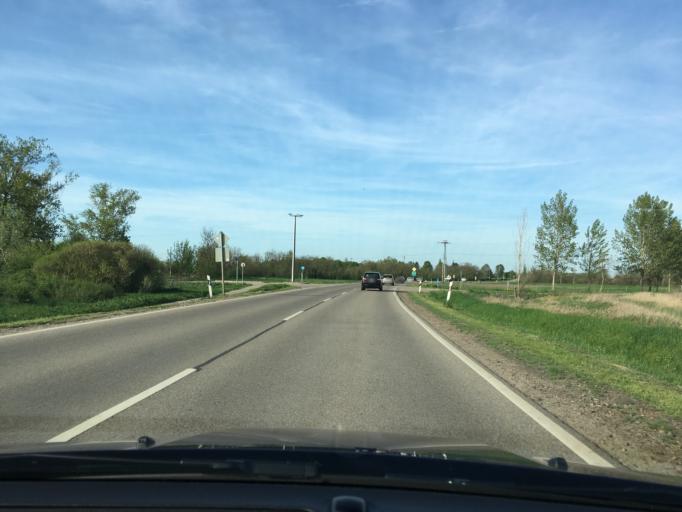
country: HU
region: Bekes
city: Mezobereny
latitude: 46.8073
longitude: 21.0079
